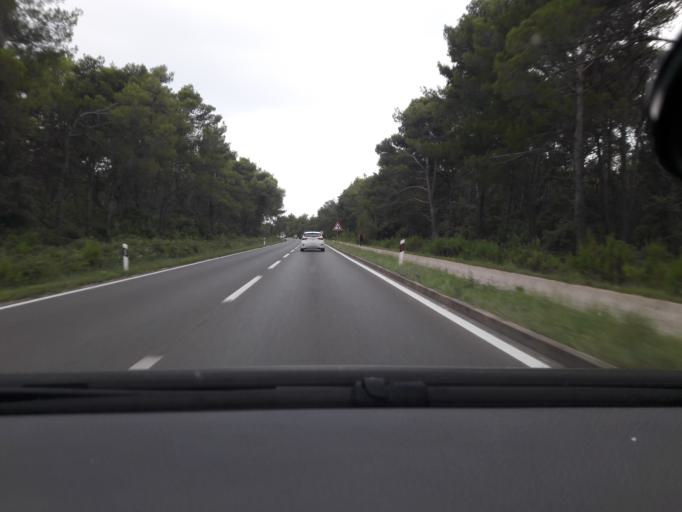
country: HR
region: Zadarska
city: Nin
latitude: 44.2015
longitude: 15.1764
